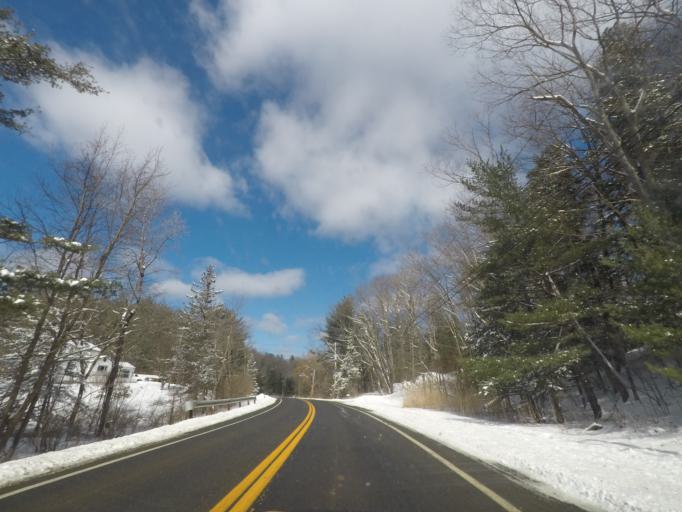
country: US
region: New York
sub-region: Rensselaer County
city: Nassau
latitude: 42.4759
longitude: -73.5227
